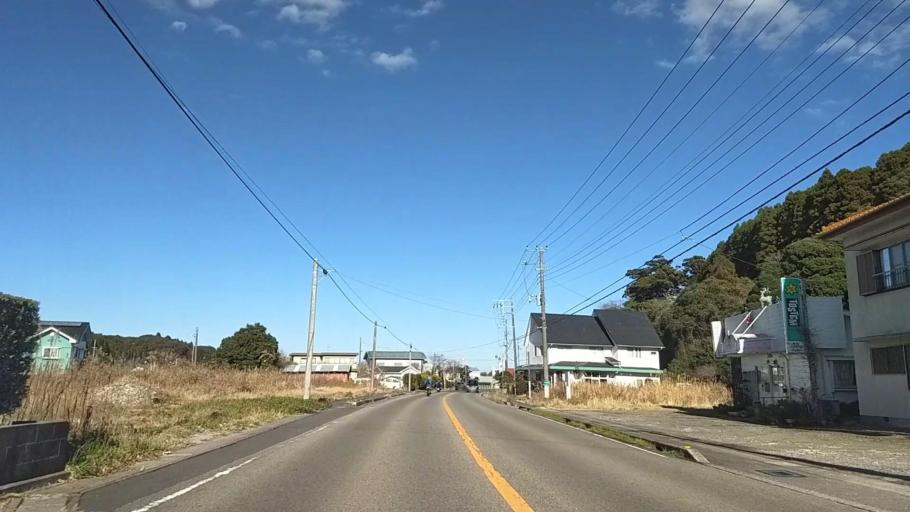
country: JP
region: Chiba
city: Ohara
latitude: 35.2174
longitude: 140.3782
